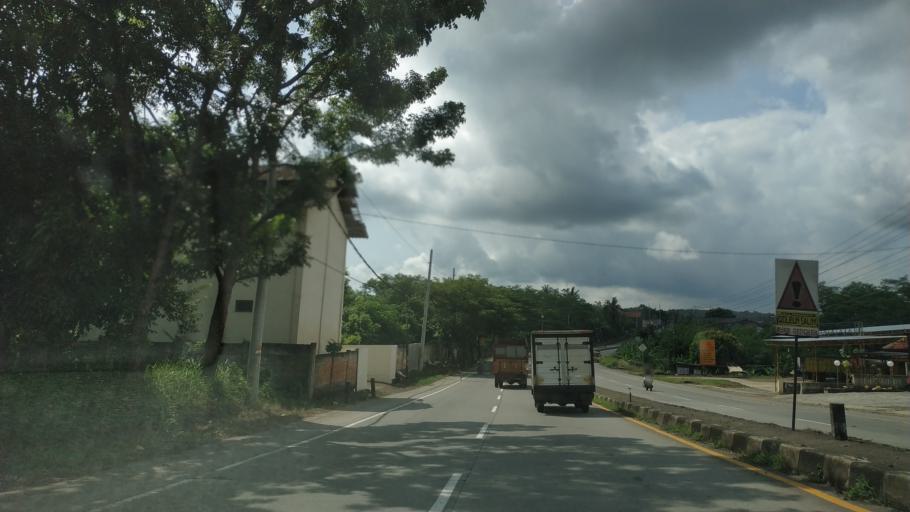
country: ID
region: Central Java
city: Pekalongan
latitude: -6.9508
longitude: 109.8285
